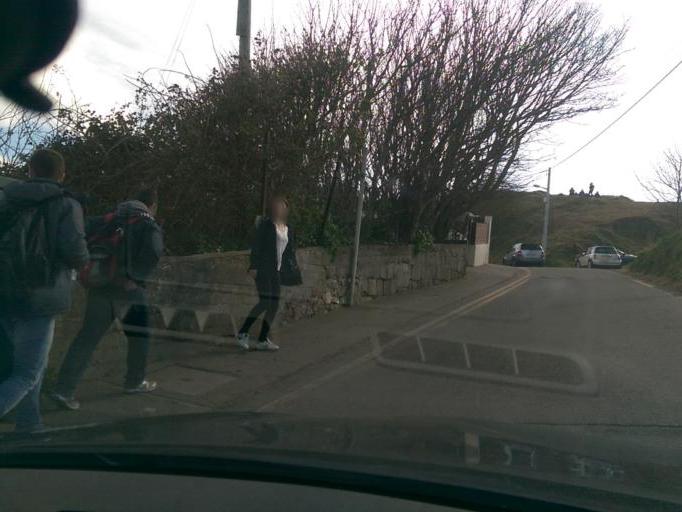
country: IE
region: Leinster
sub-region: Fingal County
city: Howth
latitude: 53.3870
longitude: -6.0635
